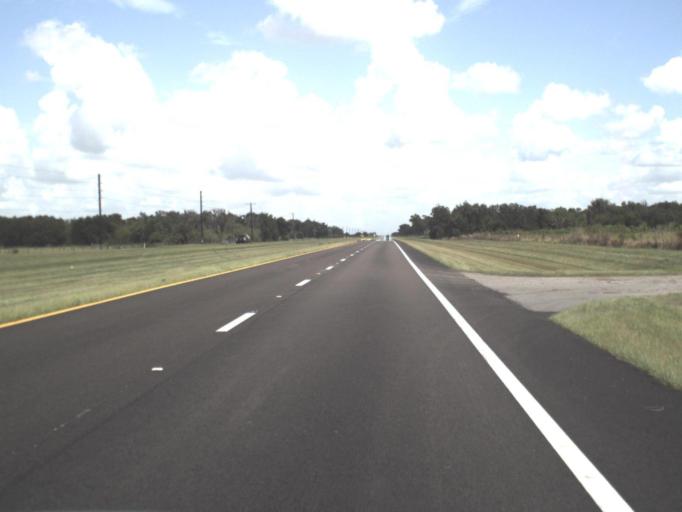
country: US
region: Florida
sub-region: Hardee County
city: Zolfo Springs
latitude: 27.4197
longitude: -81.7955
